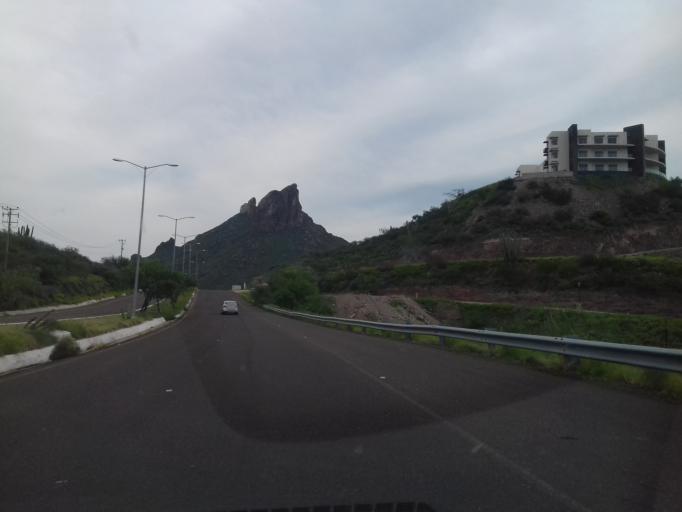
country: MX
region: Sonora
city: Heroica Guaymas
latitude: 27.9567
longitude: -111.0932
